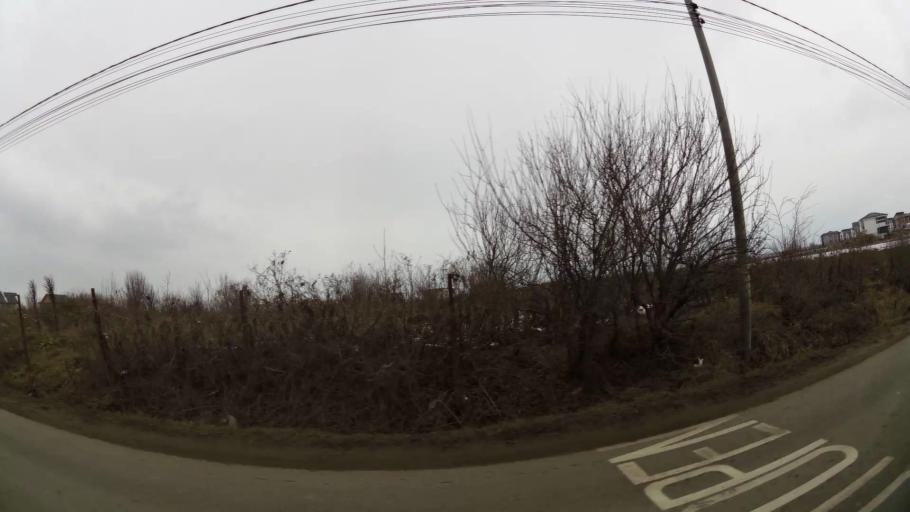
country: RO
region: Ilfov
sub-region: Comuna Otopeni
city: Otopeni
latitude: 44.5527
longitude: 26.1077
